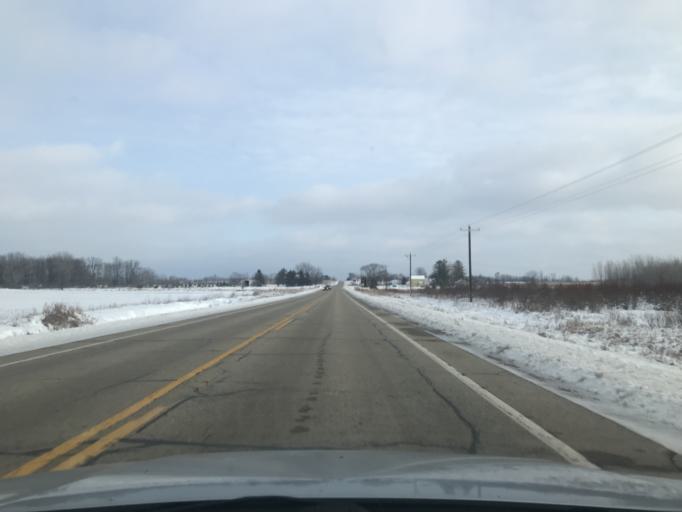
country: US
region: Wisconsin
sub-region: Oconto County
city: Oconto
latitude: 44.8932
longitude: -87.9835
